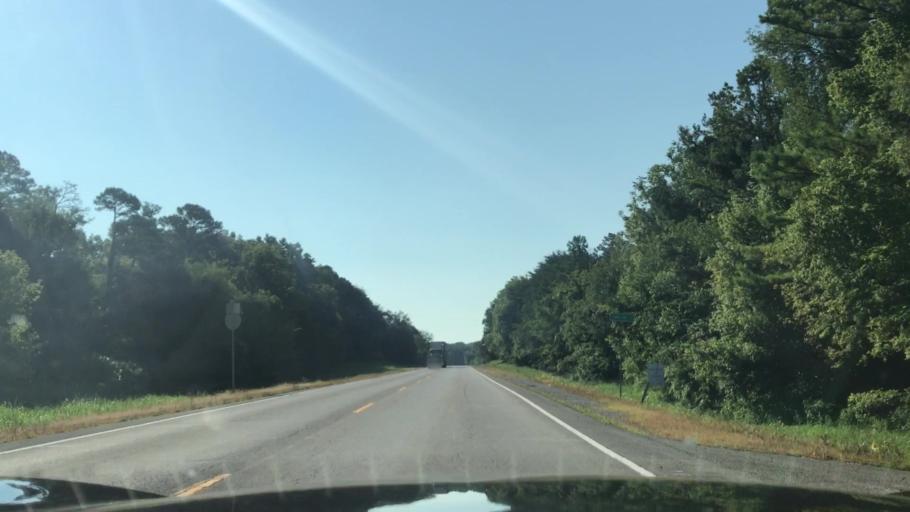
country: US
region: Kentucky
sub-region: Hart County
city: Horse Cave
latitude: 37.1986
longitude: -85.9329
